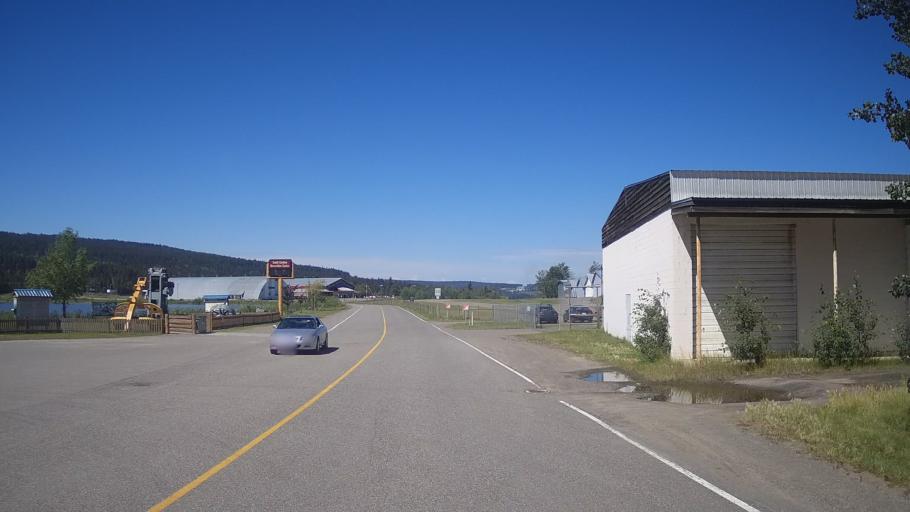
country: CA
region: British Columbia
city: Cache Creek
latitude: 51.6418
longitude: -121.2983
